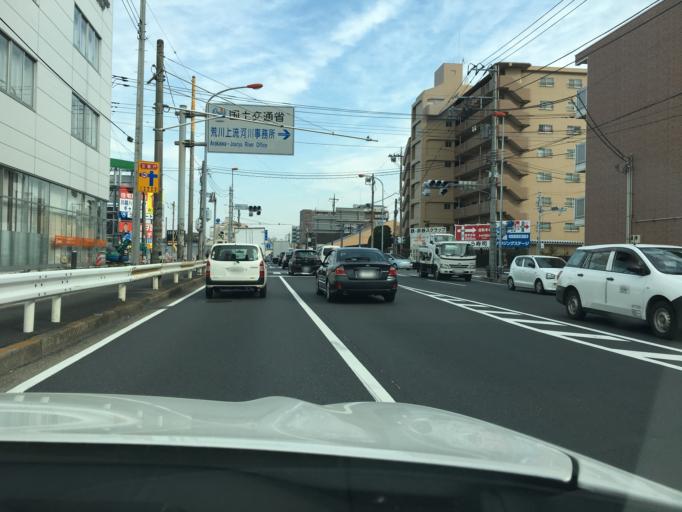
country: JP
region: Saitama
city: Kawagoe
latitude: 35.9015
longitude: 139.4810
